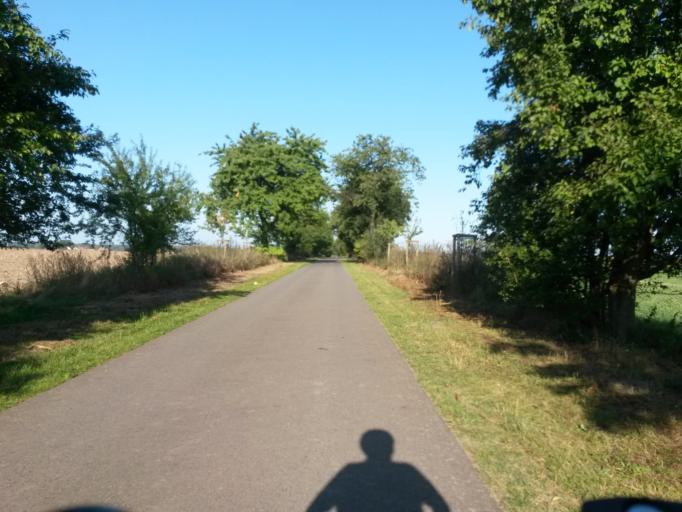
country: DE
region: Brandenburg
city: Templin
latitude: 53.1277
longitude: 13.4743
